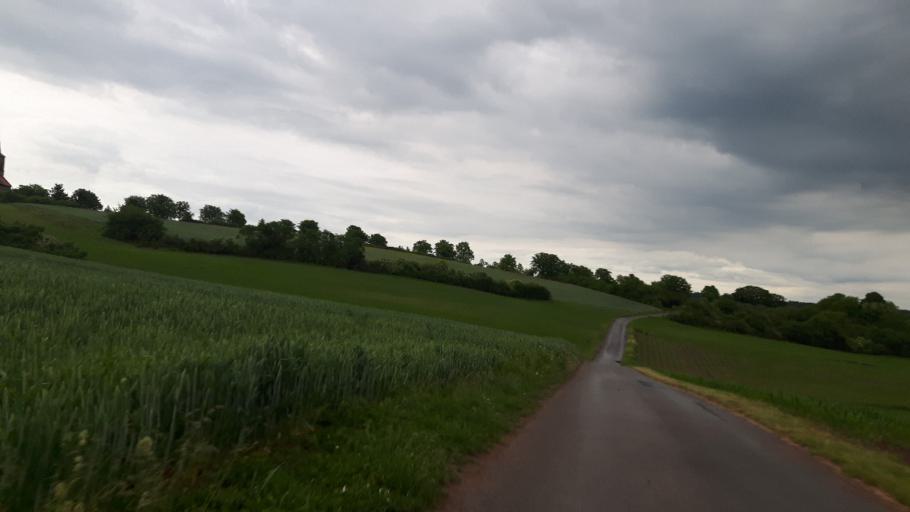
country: DE
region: Bavaria
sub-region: Regierungsbezirk Unterfranken
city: Stadtlauringen
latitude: 50.1811
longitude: 10.3622
